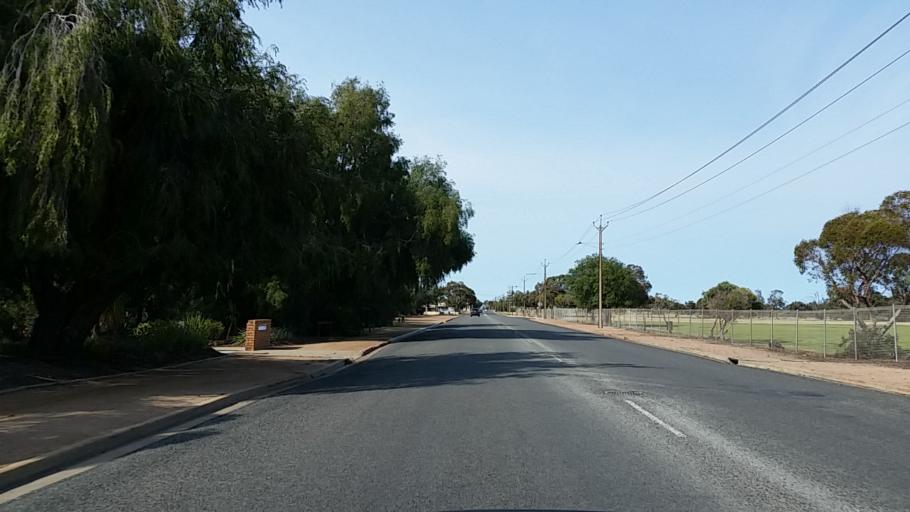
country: AU
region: South Australia
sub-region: Port Pirie City and Dists
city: Port Pirie
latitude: -33.1829
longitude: 137.9976
